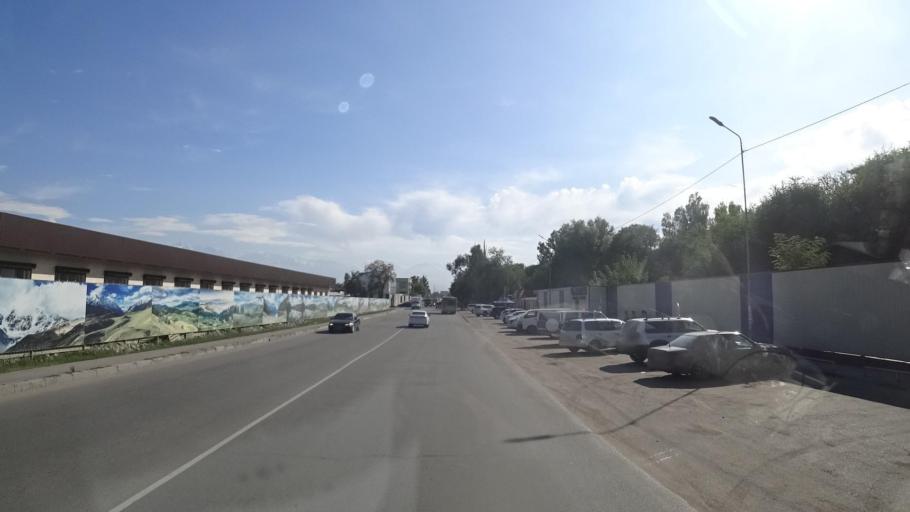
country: KZ
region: Almaty Oblysy
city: Energeticheskiy
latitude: 43.4195
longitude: 77.0219
